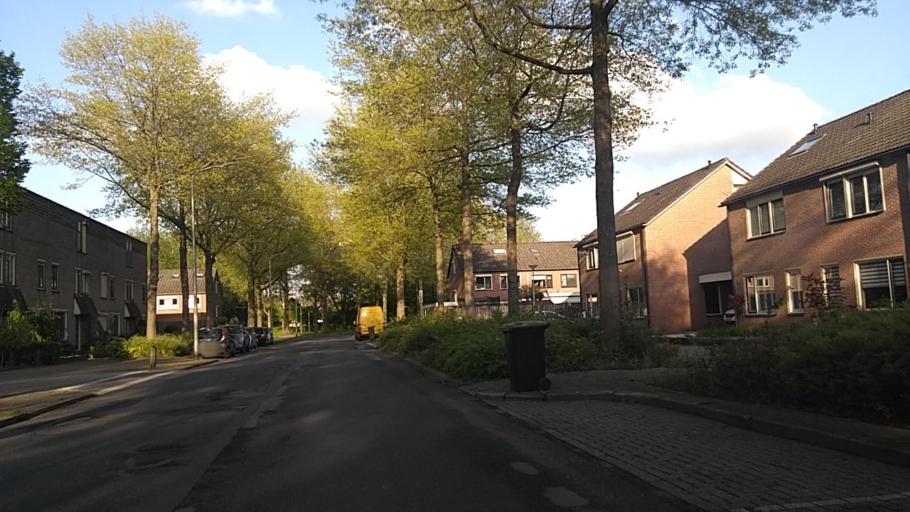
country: NL
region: Overijssel
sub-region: Gemeente Almelo
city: Almelo
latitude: 52.3334
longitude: 6.6351
